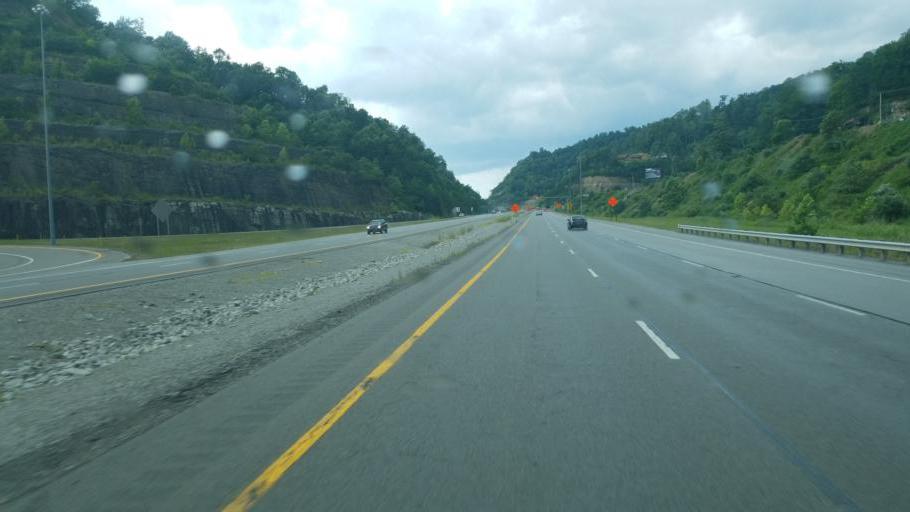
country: US
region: Kentucky
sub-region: Pike County
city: Pikeville
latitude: 37.5141
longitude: -82.4800
